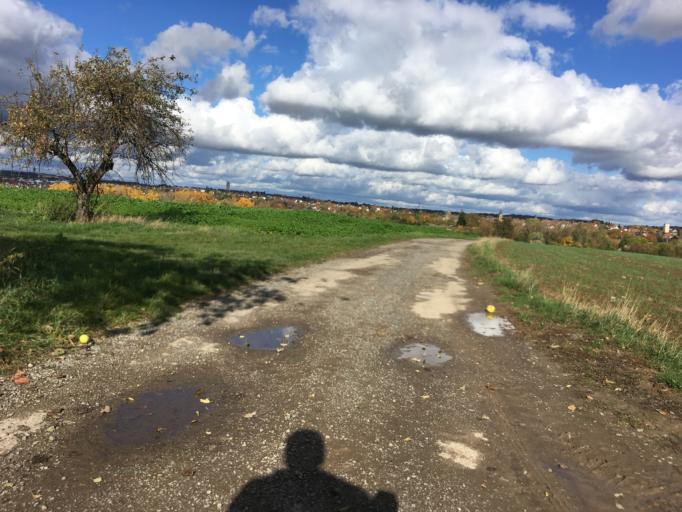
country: DE
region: Baden-Wuerttemberg
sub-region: Regierungsbezirk Stuttgart
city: Neuenstein
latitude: 49.1929
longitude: 9.5752
